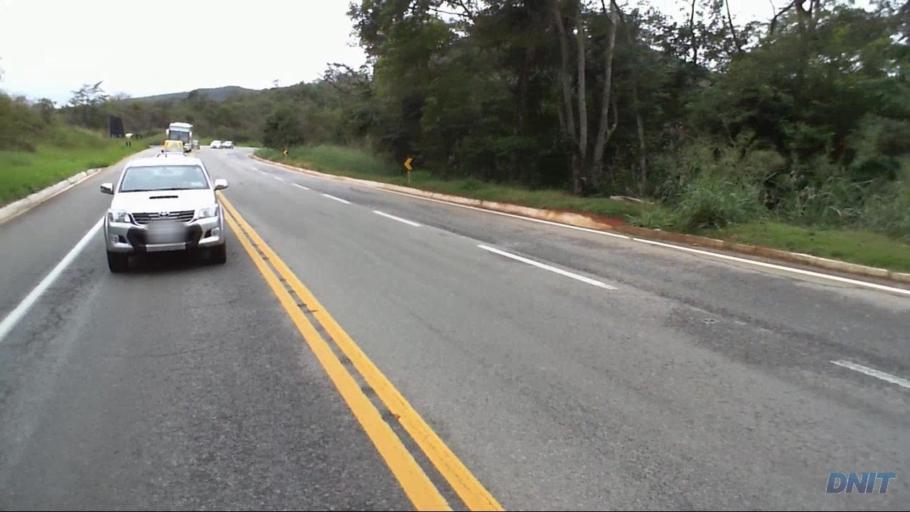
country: BR
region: Minas Gerais
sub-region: Joao Monlevade
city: Joao Monlevade
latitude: -19.8423
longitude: -43.3194
